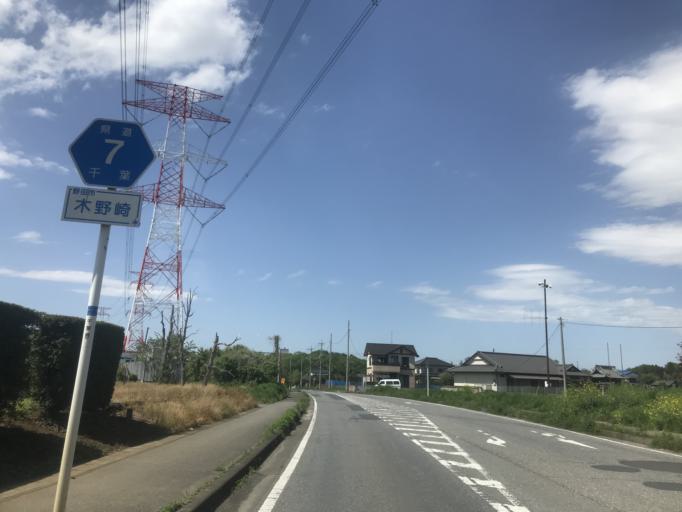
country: JP
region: Chiba
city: Noda
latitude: 35.9557
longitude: 139.9103
